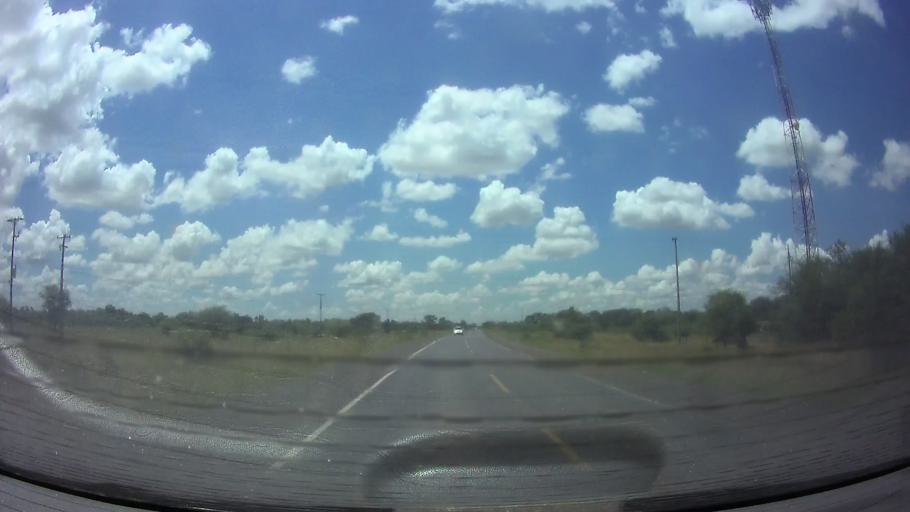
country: PY
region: Presidente Hayes
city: Nanawa
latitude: -25.2243
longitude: -57.6831
